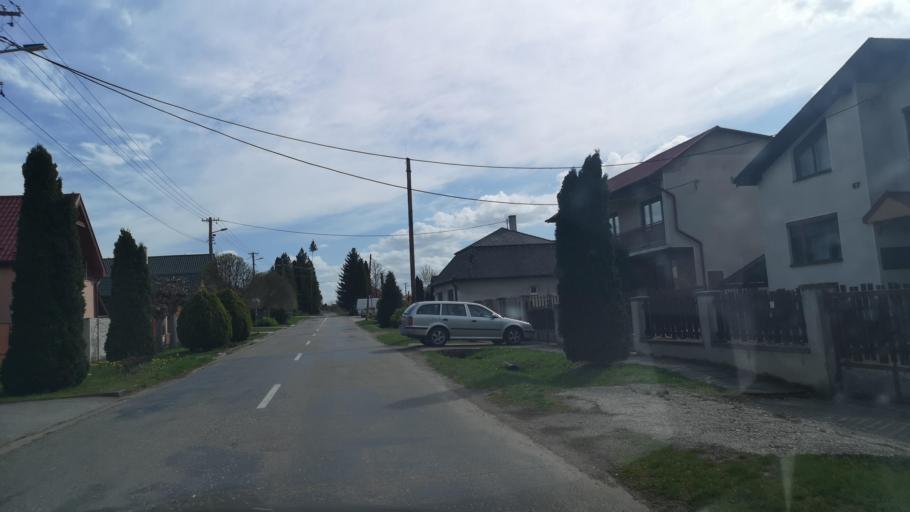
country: SK
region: Nitriansky
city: Zlate Moravce
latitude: 48.3181
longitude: 18.3601
